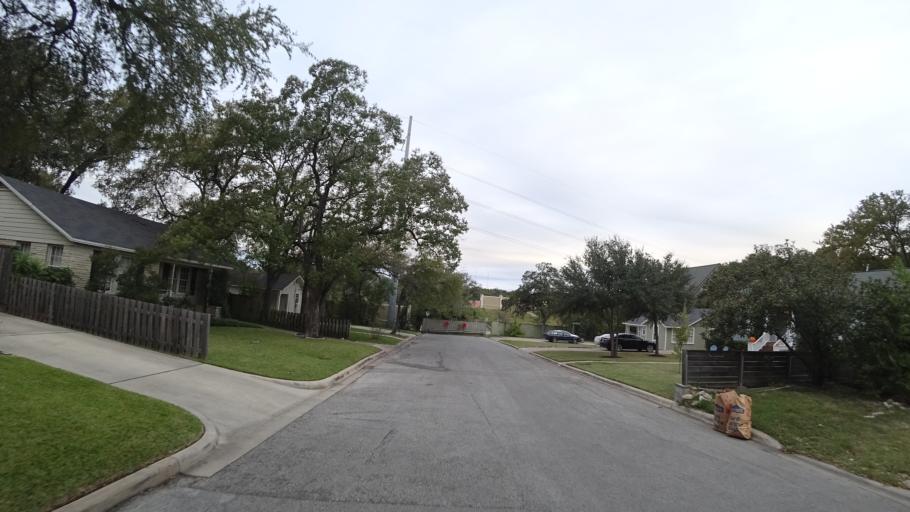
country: US
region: Texas
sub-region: Travis County
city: Austin
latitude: 30.2995
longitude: -97.7572
